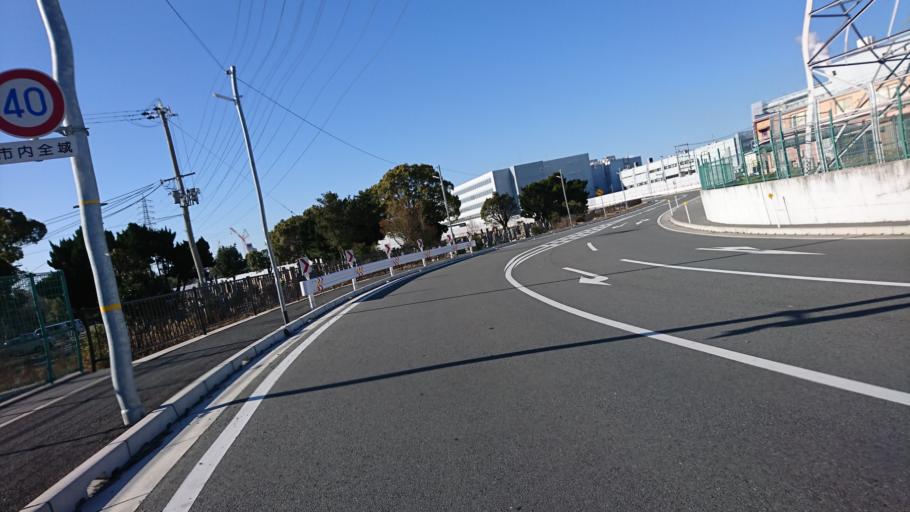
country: JP
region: Hyogo
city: Kakogawacho-honmachi
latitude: 34.7526
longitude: 134.7931
